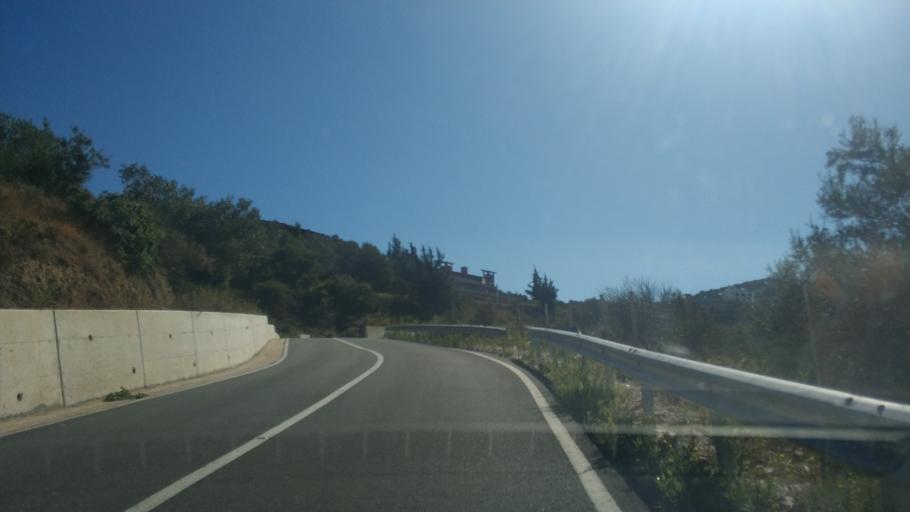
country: AL
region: Vlore
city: Vlore
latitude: 40.4568
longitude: 19.5131
